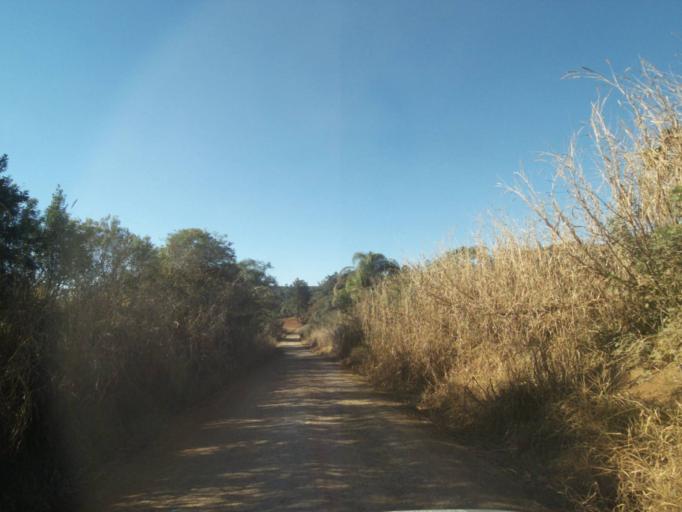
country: BR
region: Parana
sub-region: Tibagi
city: Tibagi
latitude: -24.5322
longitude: -50.4937
